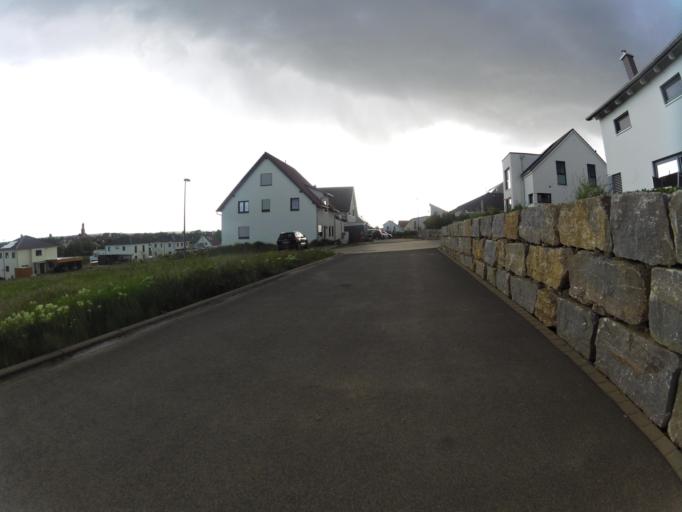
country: DE
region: Bavaria
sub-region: Regierungsbezirk Unterfranken
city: Volkach
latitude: 49.8707
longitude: 10.2334
